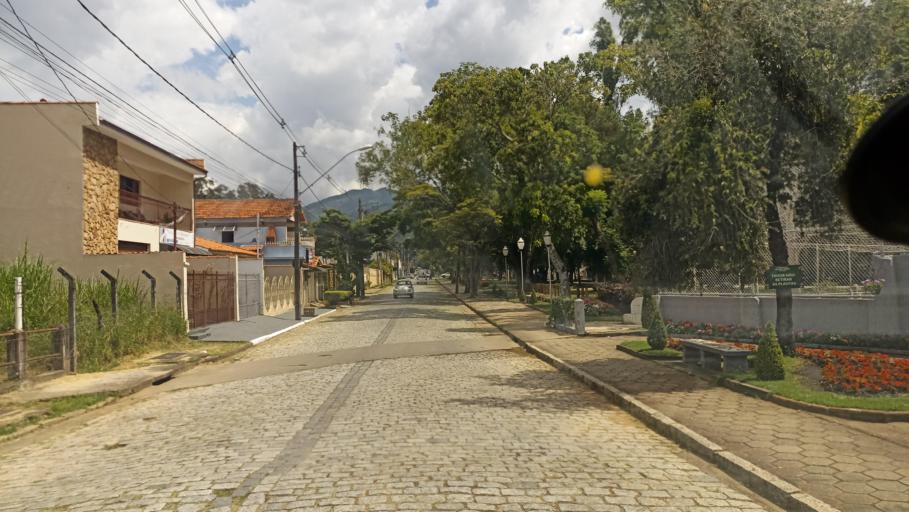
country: BR
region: Minas Gerais
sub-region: Passa Quatro
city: Passa Quatro
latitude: -22.3954
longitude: -44.9665
